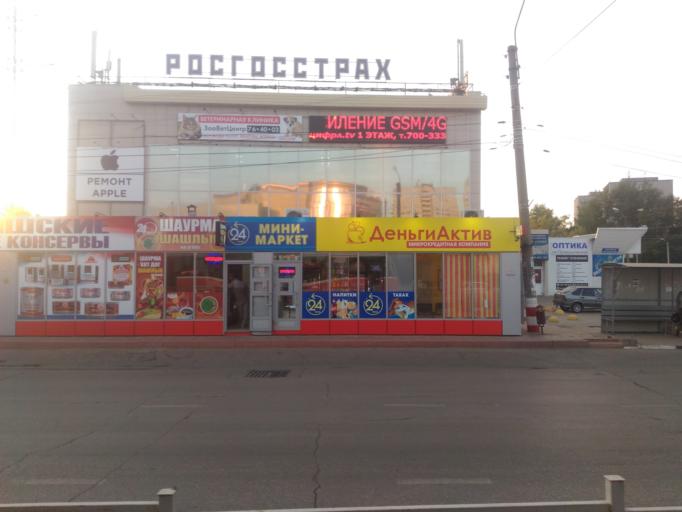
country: RU
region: Ulyanovsk
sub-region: Ulyanovskiy Rayon
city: Ulyanovsk
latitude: 54.2849
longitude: 48.3015
